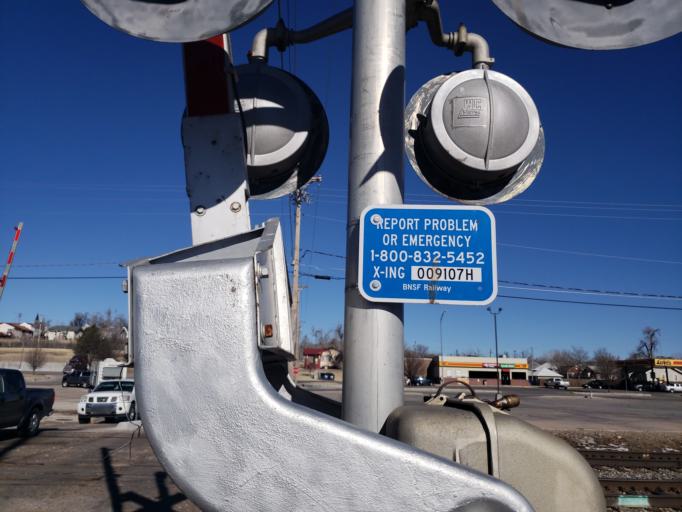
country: US
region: Kansas
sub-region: Ford County
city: Dodge City
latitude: 37.7527
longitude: -100.0293
